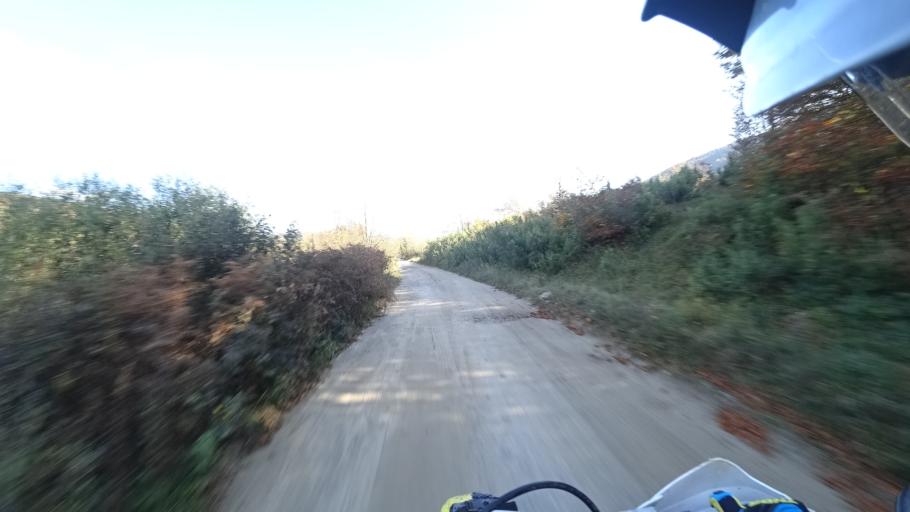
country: HR
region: Karlovacka
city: Plaski
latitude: 45.0404
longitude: 15.3783
